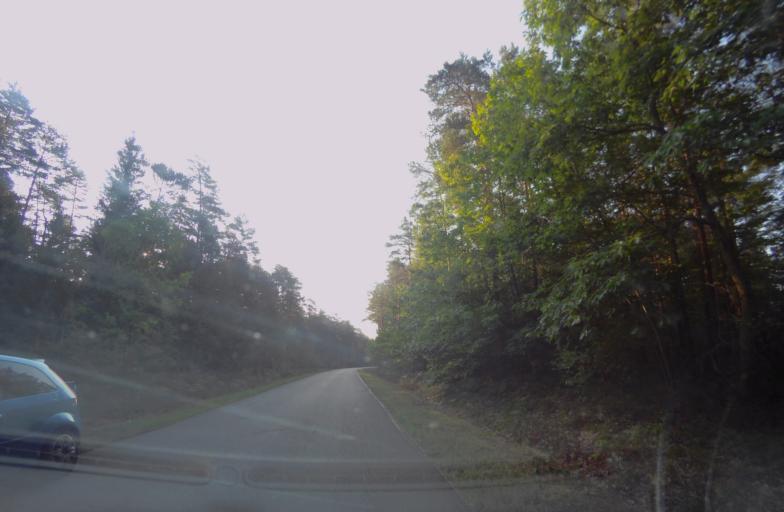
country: PL
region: Subcarpathian Voivodeship
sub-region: Powiat nizanski
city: Harasiuki
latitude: 50.5870
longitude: 22.5090
